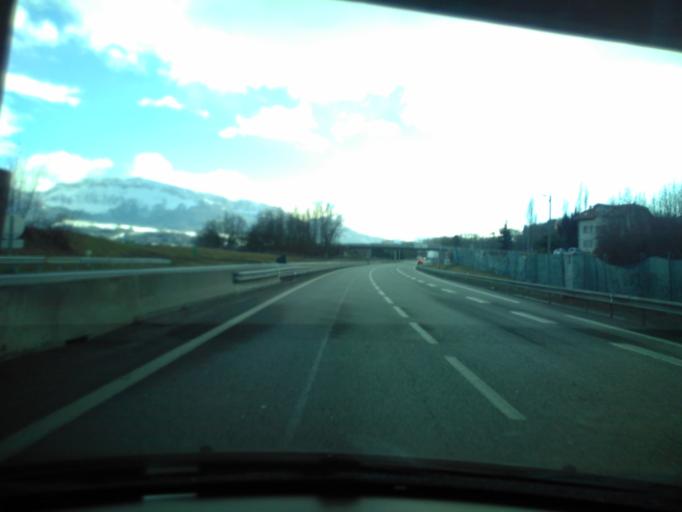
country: FR
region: Rhone-Alpes
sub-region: Departement de la Haute-Savoie
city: Etaux
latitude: 46.0749
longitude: 6.2907
